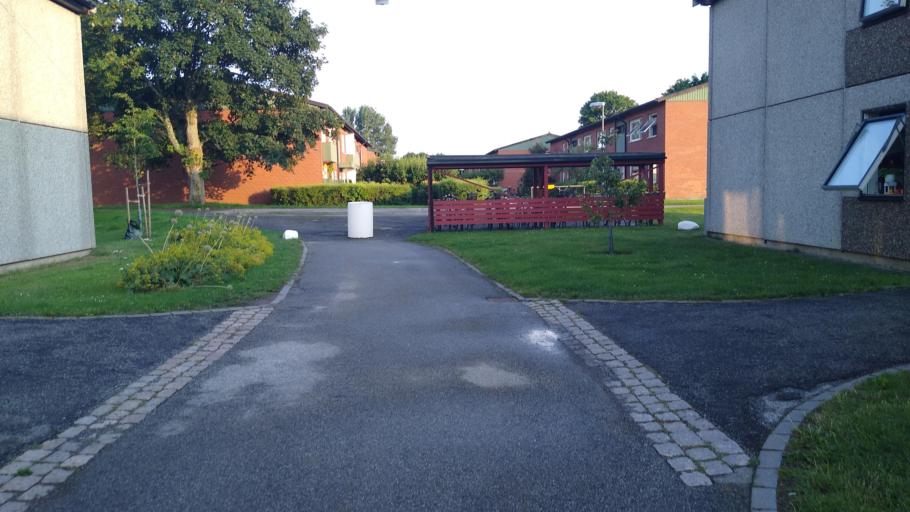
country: SE
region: Skane
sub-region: Lunds Kommun
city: Lund
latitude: 55.7261
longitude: 13.1786
